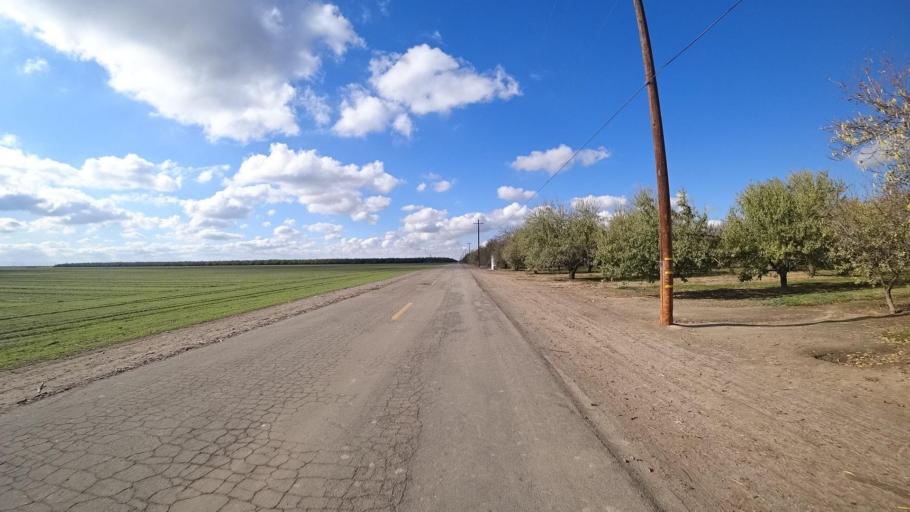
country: US
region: California
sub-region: Kern County
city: McFarland
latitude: 35.6815
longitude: -119.2624
